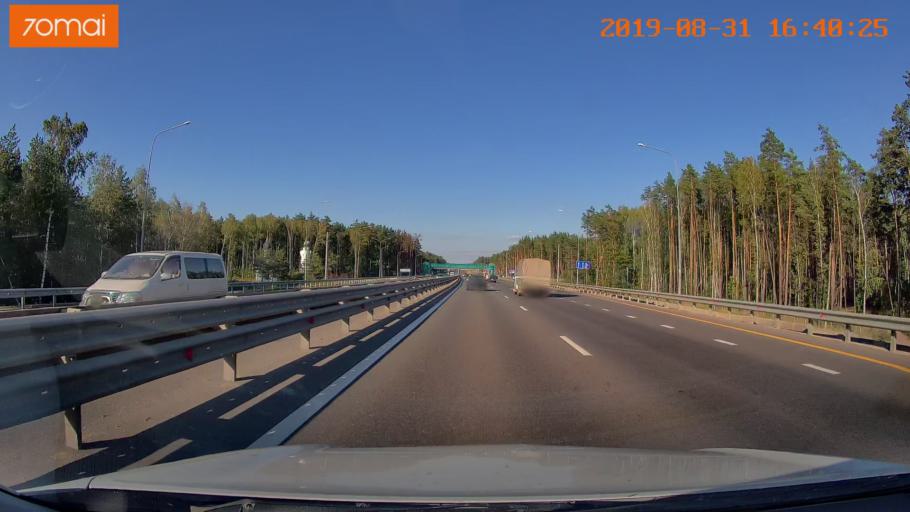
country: RU
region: Kaluga
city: Kurovskoye
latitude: 54.5651
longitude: 36.0484
